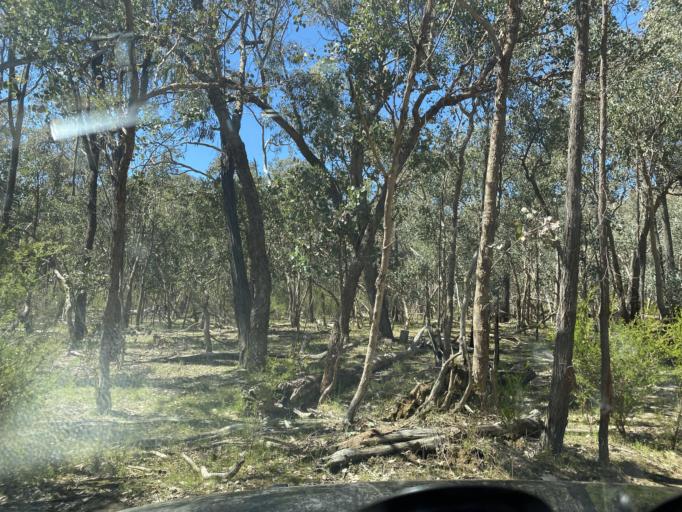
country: AU
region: Victoria
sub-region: Benalla
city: Benalla
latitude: -36.7030
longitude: 146.1523
